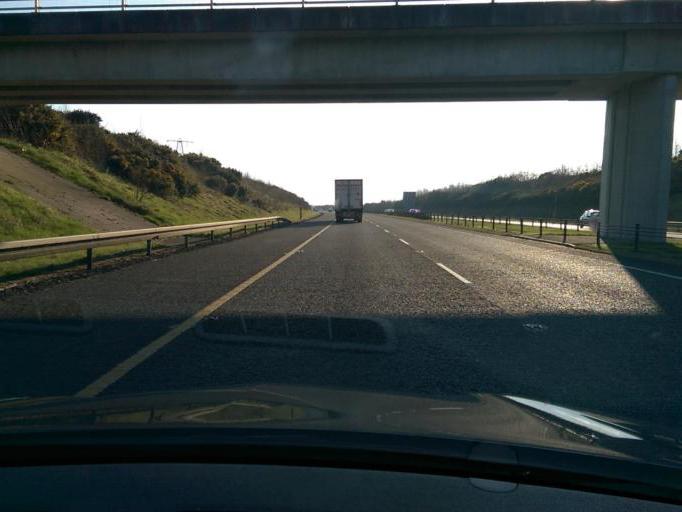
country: IE
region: Leinster
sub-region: Laois
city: Stradbally
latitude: 53.0790
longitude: -7.1974
